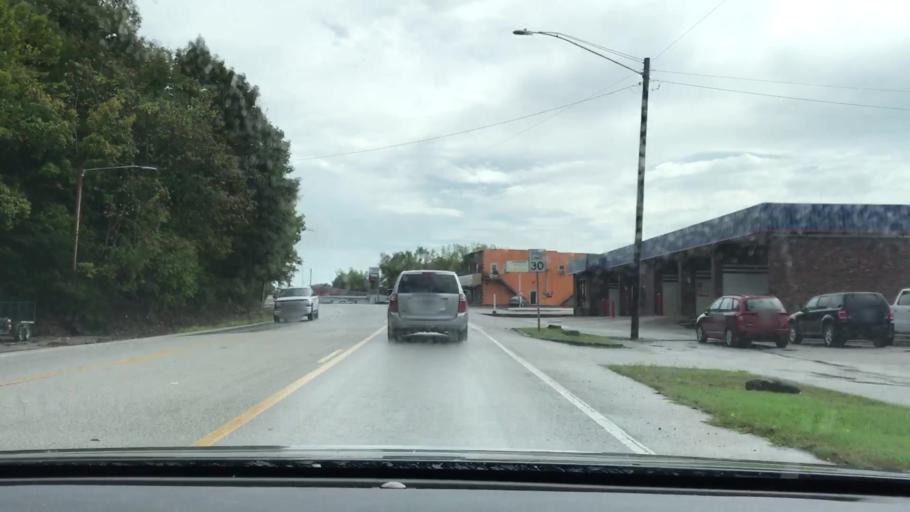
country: US
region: Tennessee
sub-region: Smith County
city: Carthage
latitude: 36.2638
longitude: -85.9559
